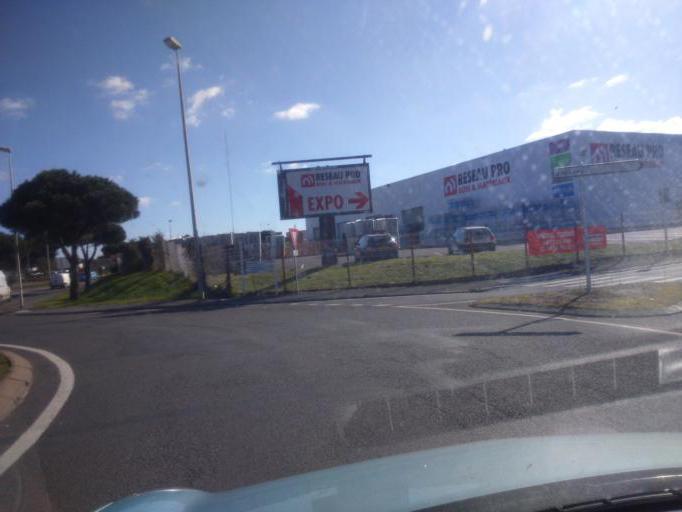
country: FR
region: Pays de la Loire
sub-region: Departement de la Loire-Atlantique
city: Guerande
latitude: 47.3272
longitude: -2.4132
